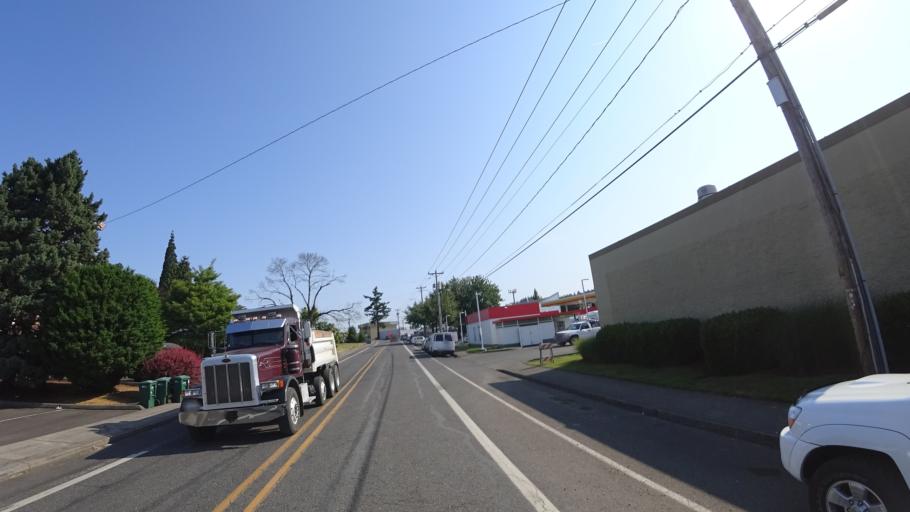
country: US
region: Oregon
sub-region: Clackamas County
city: Oatfield
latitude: 45.4450
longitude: -122.5801
